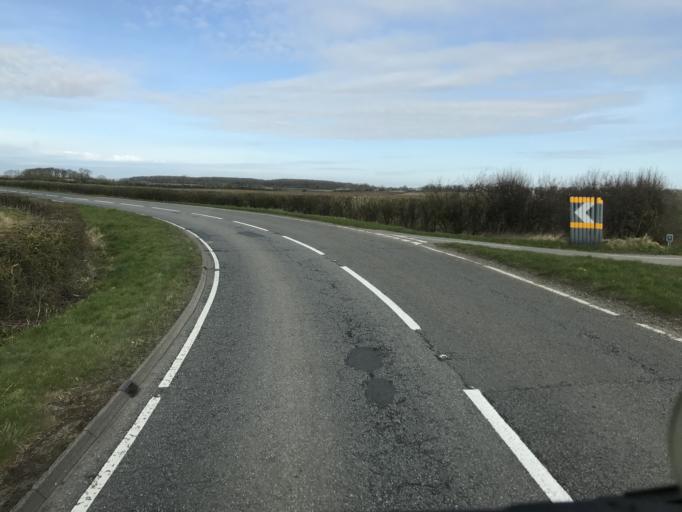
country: GB
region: England
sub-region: Lincolnshire
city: Market Rasen
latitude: 53.3950
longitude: -0.4062
